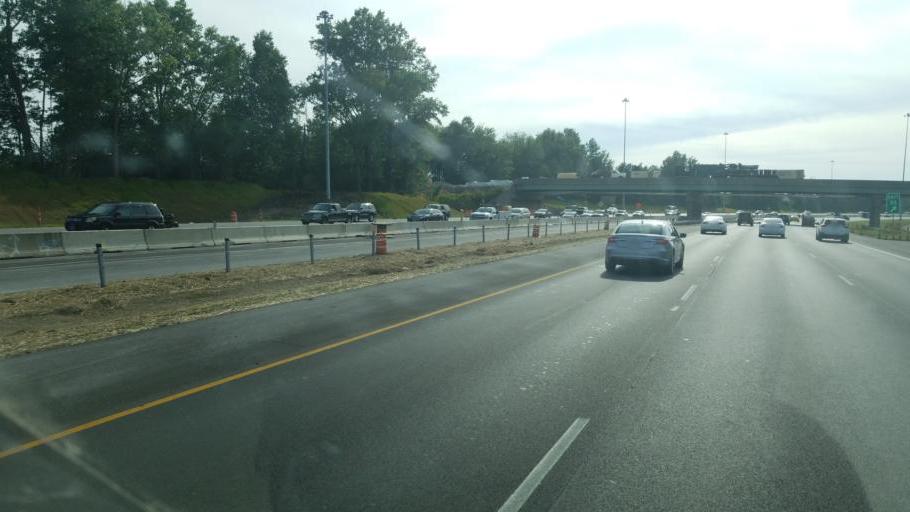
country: US
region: Ohio
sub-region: Franklin County
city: Gahanna
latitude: 40.0086
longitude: -82.8928
